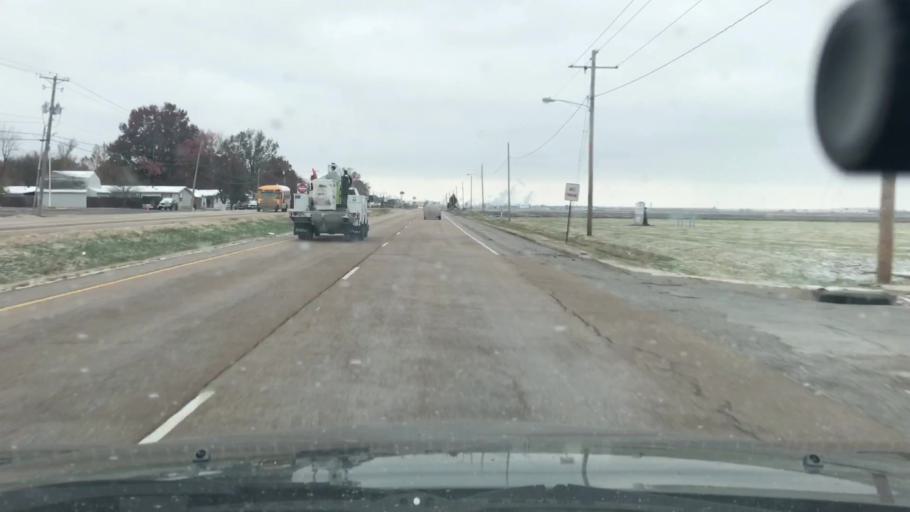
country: US
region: Illinois
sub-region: Madison County
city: Pontoon Beach
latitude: 38.7341
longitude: -90.0709
